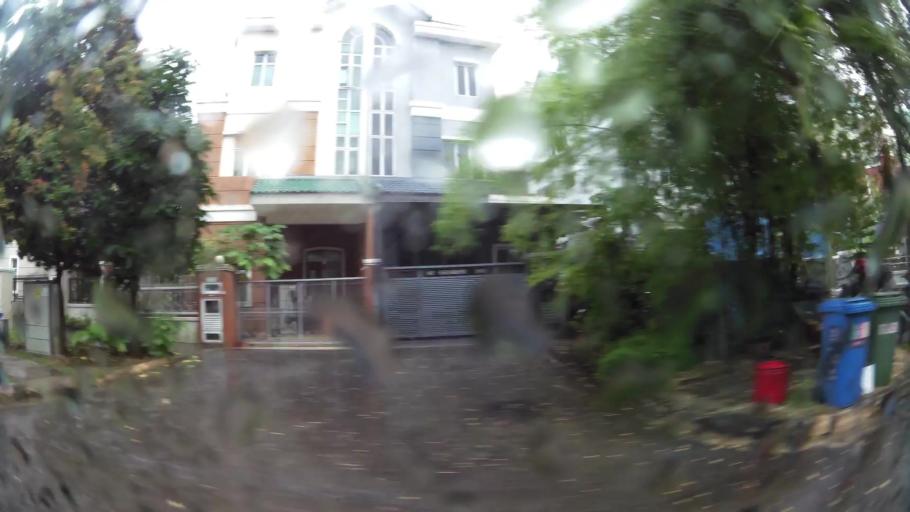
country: MY
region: Johor
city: Kampung Pasir Gudang Baru
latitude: 1.3869
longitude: 103.8577
